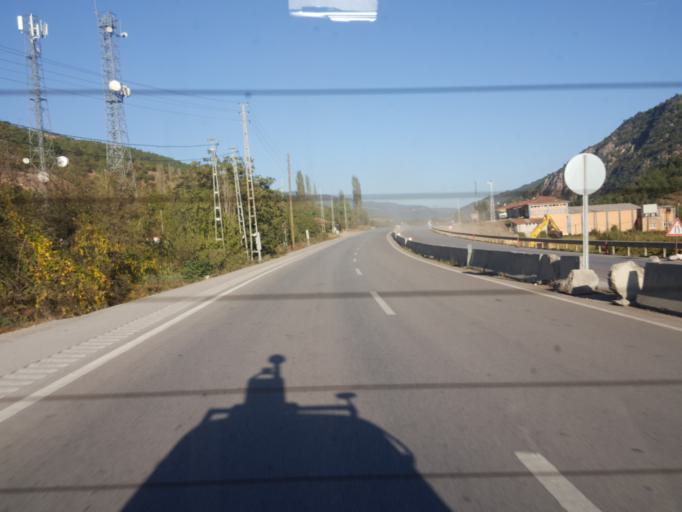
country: TR
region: Amasya
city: Akdag
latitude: 40.7434
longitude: 35.9961
